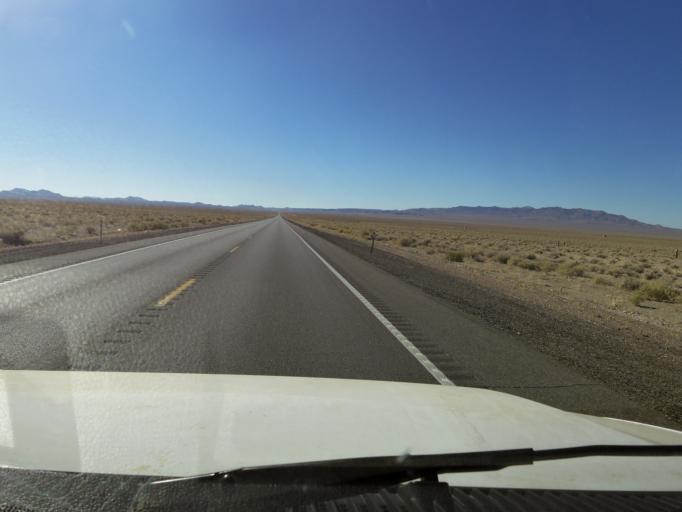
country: US
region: Nevada
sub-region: Esmeralda County
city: Goldfield
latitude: 37.8815
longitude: -117.2425
